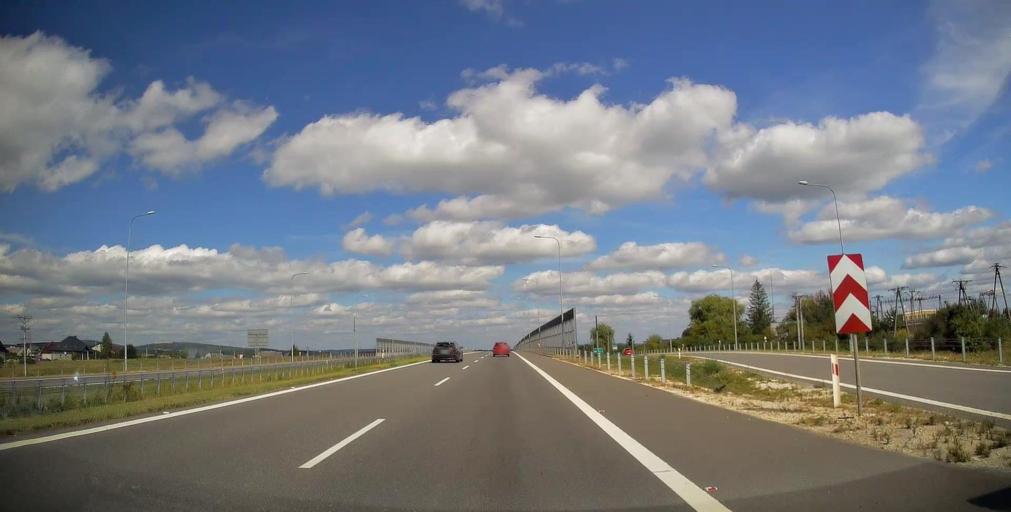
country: PL
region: Swietokrzyskie
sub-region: Powiat kielecki
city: Checiny
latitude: 50.7537
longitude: 20.4559
